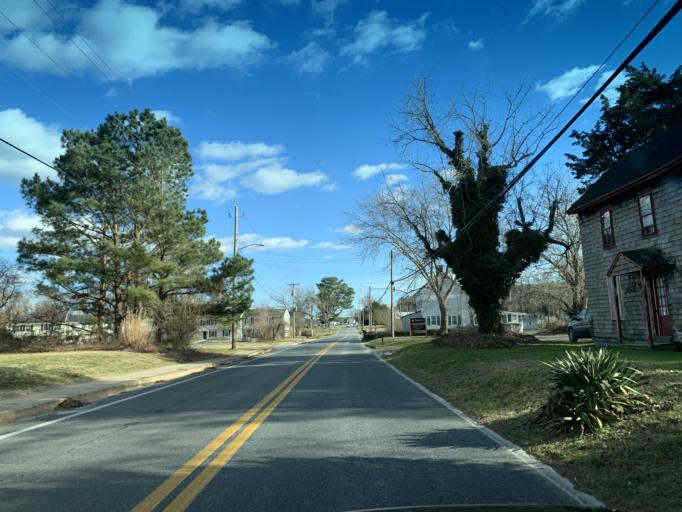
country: US
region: Maryland
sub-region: Worcester County
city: Berlin
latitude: 38.3227
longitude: -75.2065
